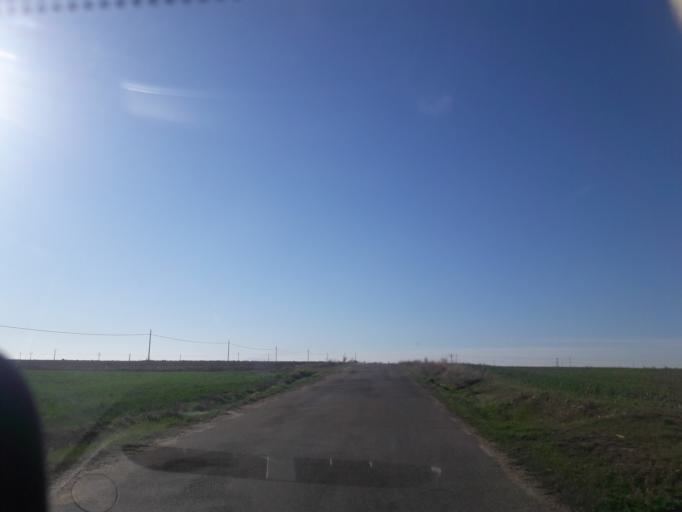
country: ES
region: Castille and Leon
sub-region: Provincia de Salamanca
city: Penarandilla
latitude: 40.8734
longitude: -5.3896
